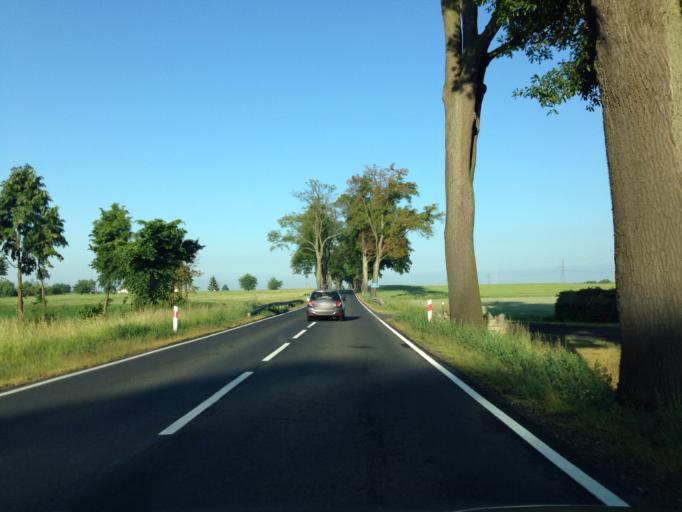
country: PL
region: Kujawsko-Pomorskie
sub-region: Powiat grudziadzki
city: Rogozno
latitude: 53.5791
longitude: 18.8887
